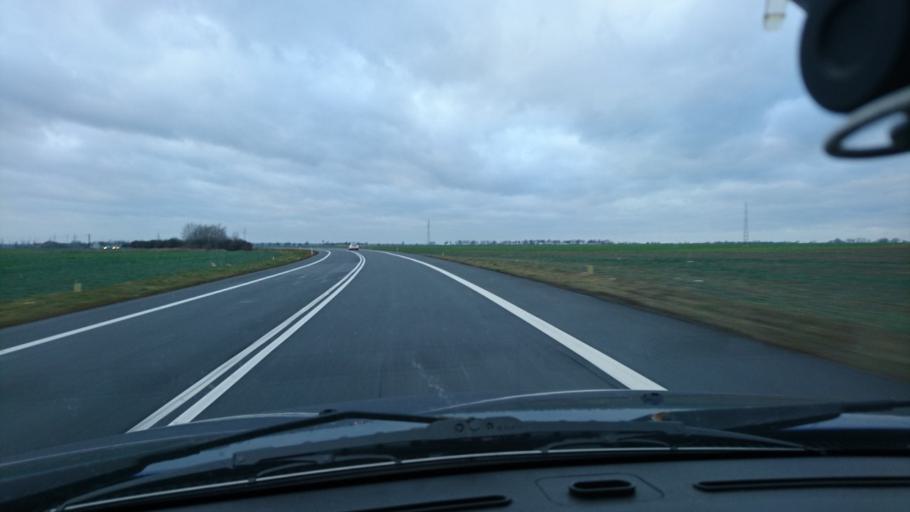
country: PL
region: Opole Voivodeship
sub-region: Powiat kluczborski
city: Kluczbork
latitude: 50.9878
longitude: 18.2361
